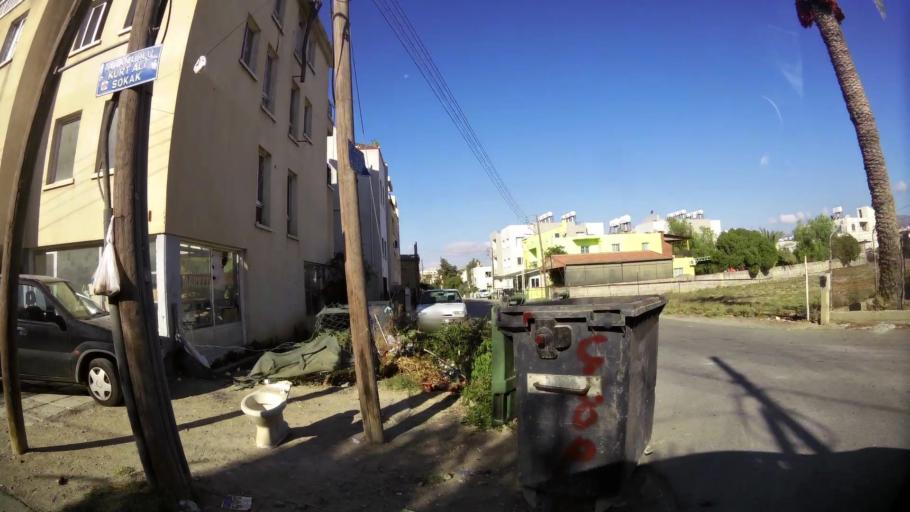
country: CY
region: Lefkosia
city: Nicosia
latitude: 35.2150
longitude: 33.3016
